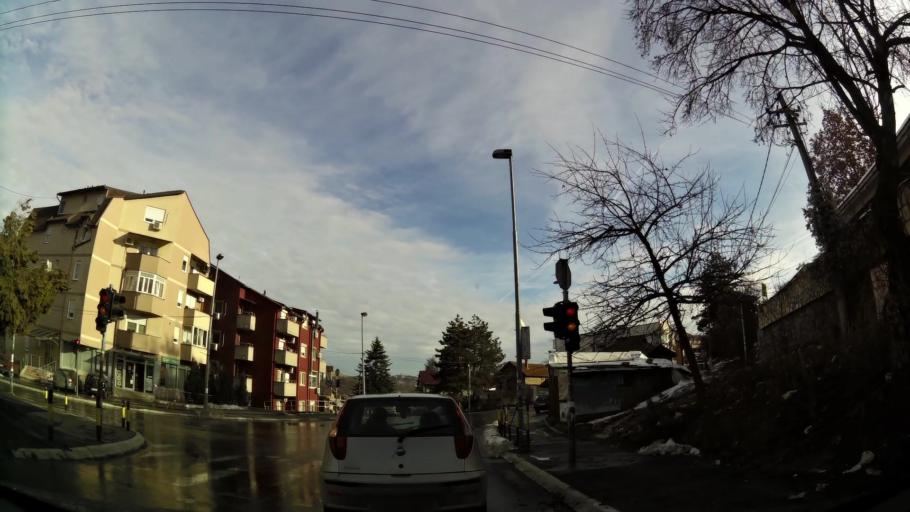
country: RS
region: Central Serbia
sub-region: Belgrade
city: Rakovica
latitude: 44.7331
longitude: 20.4270
